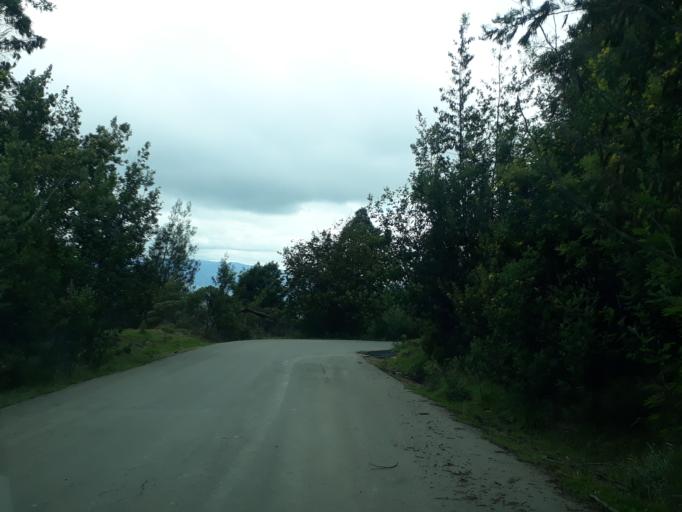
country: CO
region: Cundinamarca
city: Cucunuba
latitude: 5.2100
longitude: -73.7854
